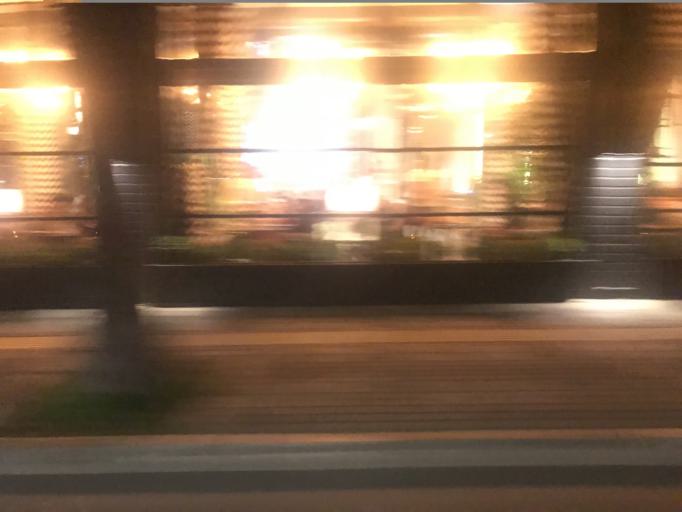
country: TR
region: Istanbul
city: Bahcelievler
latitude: 40.9635
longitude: 28.8392
